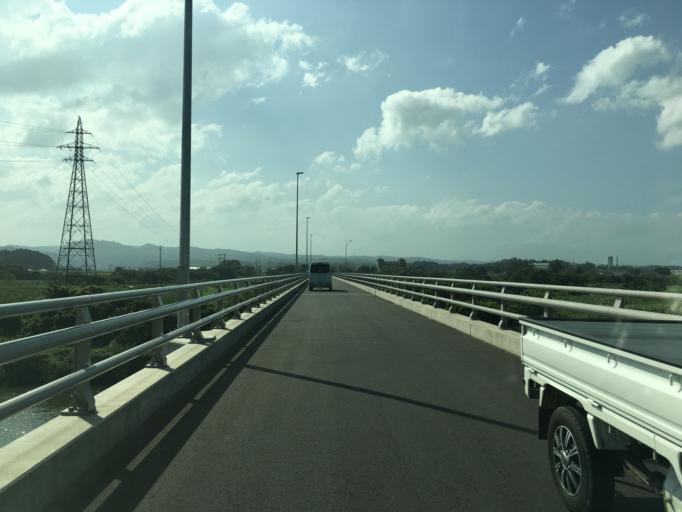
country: JP
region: Miyagi
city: Kakuda
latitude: 37.9594
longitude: 140.7912
